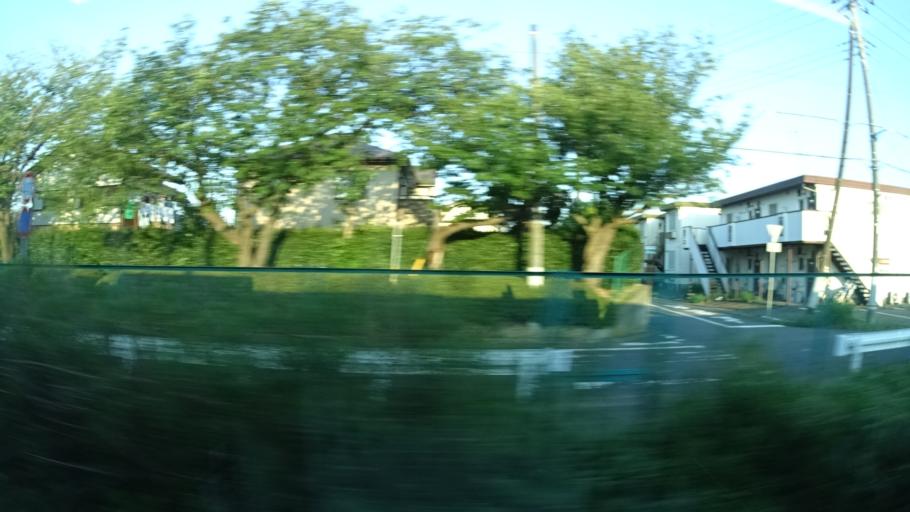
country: JP
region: Ibaraki
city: Ushiku
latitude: 35.9890
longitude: 140.1469
